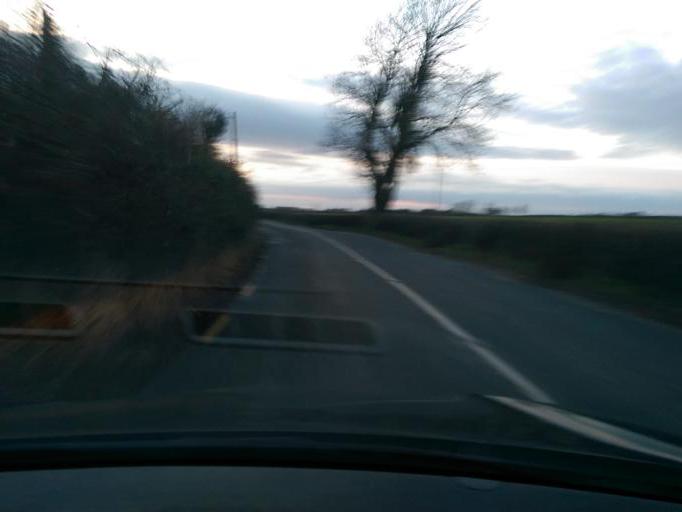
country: IE
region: Leinster
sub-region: Uibh Fhaili
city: Banagher
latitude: 53.1077
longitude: -8.0695
